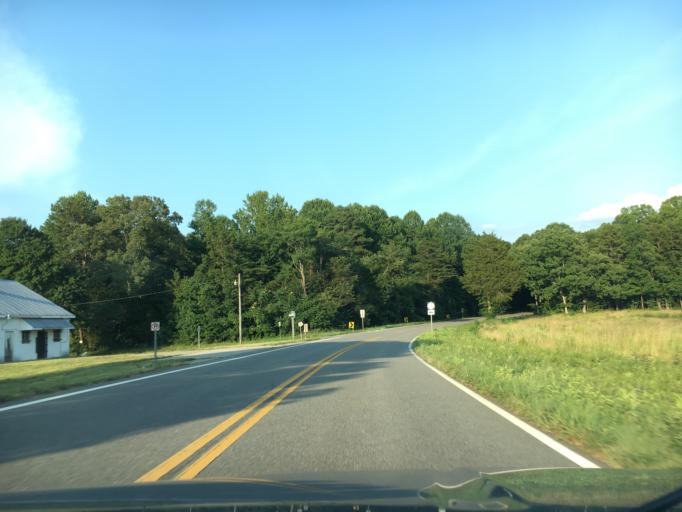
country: US
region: Virginia
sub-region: Halifax County
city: Mountain Road
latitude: 36.8354
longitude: -79.1309
